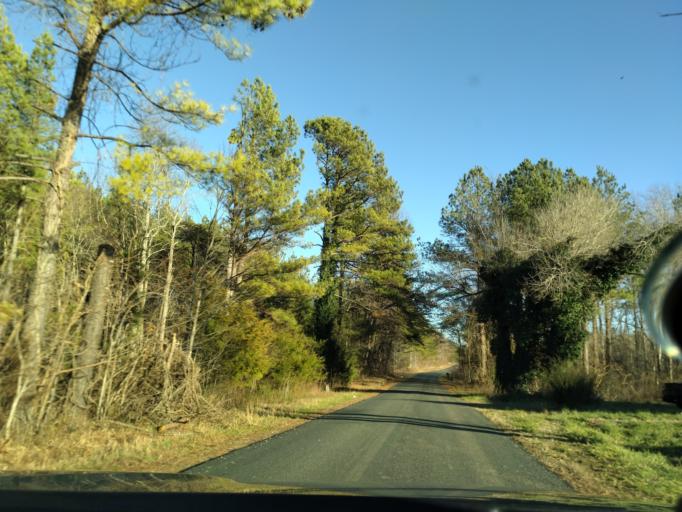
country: US
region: Virginia
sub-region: Buckingham County
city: Buckingham
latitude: 37.3708
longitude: -78.6219
